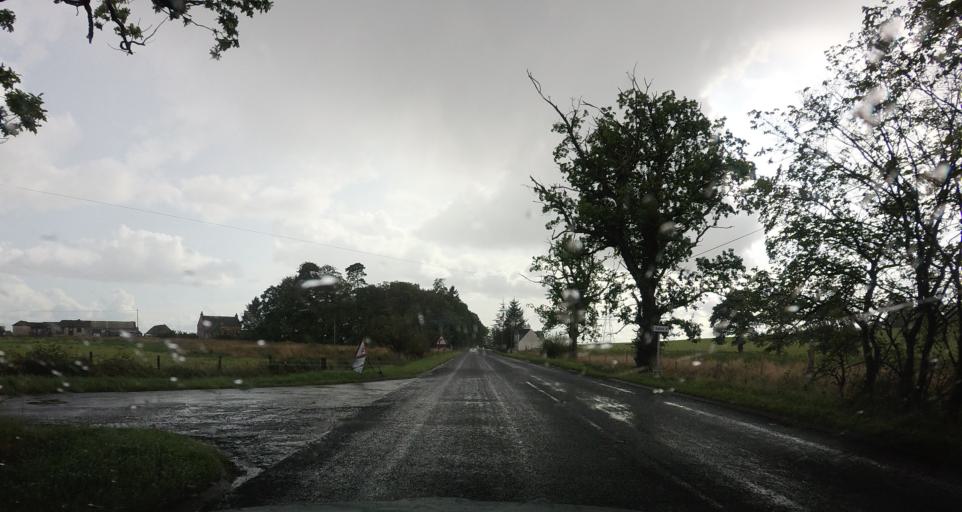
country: GB
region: Scotland
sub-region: Clackmannanshire
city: Dollar
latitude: 56.1367
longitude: -3.6523
